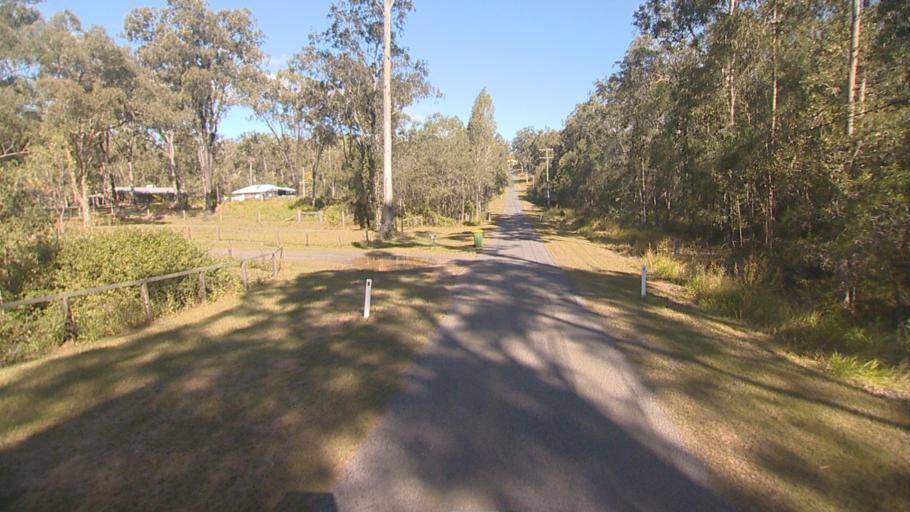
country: AU
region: Queensland
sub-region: Logan
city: Chambers Flat
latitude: -27.8176
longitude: 153.0771
